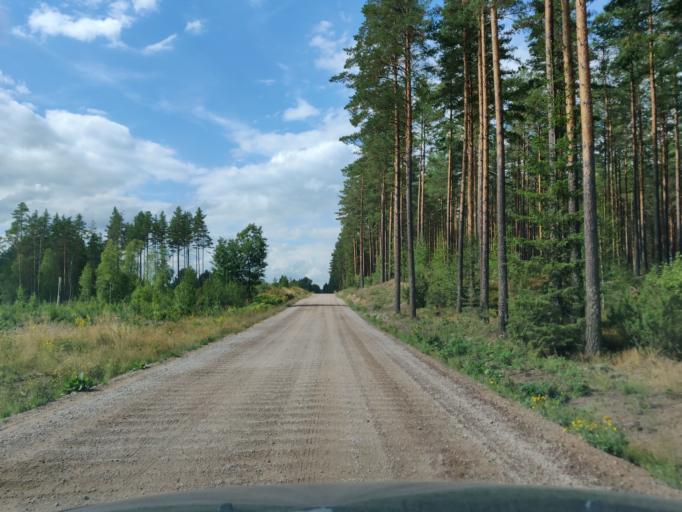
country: SE
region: Vaermland
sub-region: Munkfors Kommun
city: Munkfors
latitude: 59.9743
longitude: 13.5373
